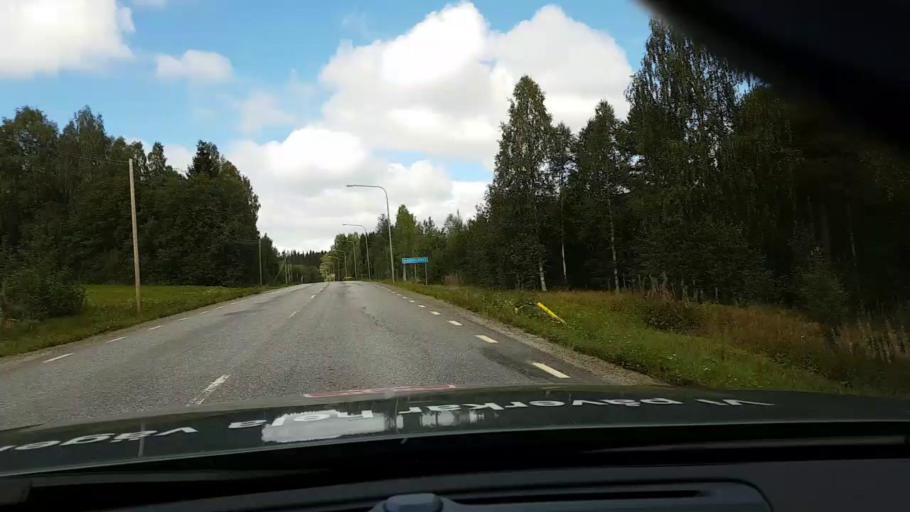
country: SE
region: Vaesternorrland
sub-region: OErnskoeldsviks Kommun
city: Bredbyn
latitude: 63.4878
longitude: 18.0845
